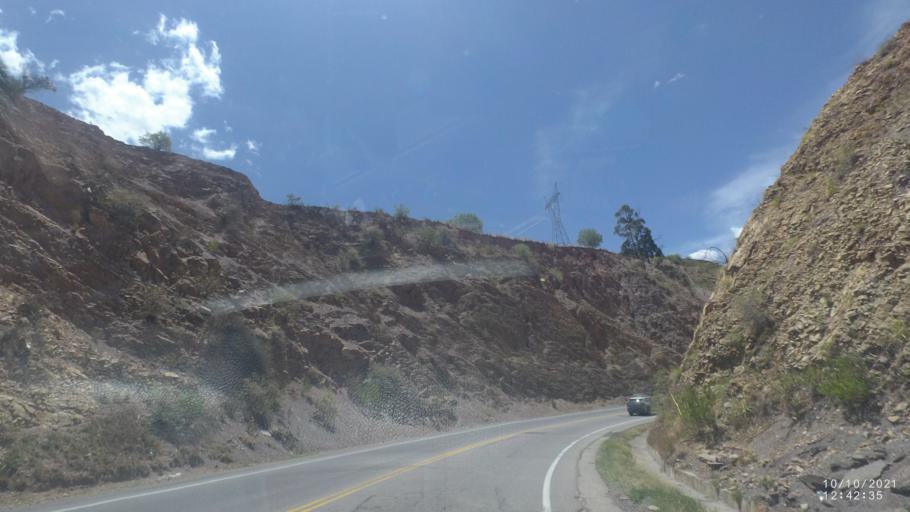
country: BO
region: Cochabamba
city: Irpa Irpa
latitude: -17.6282
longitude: -66.3936
